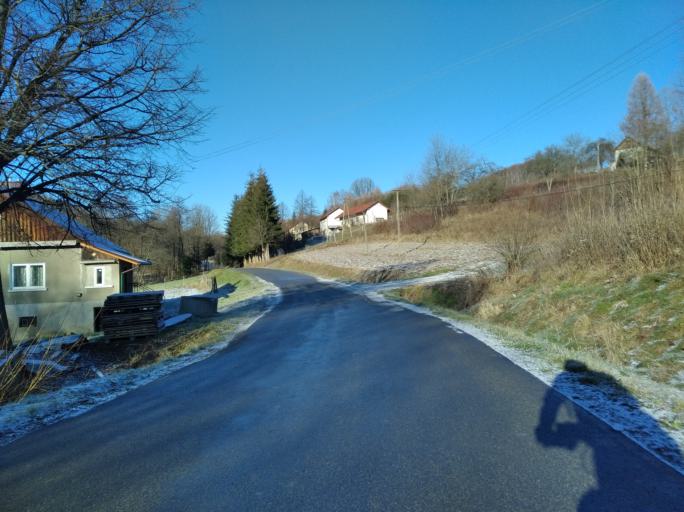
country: PL
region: Subcarpathian Voivodeship
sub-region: Powiat ropczycko-sedziszowski
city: Iwierzyce
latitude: 49.9569
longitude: 21.7642
